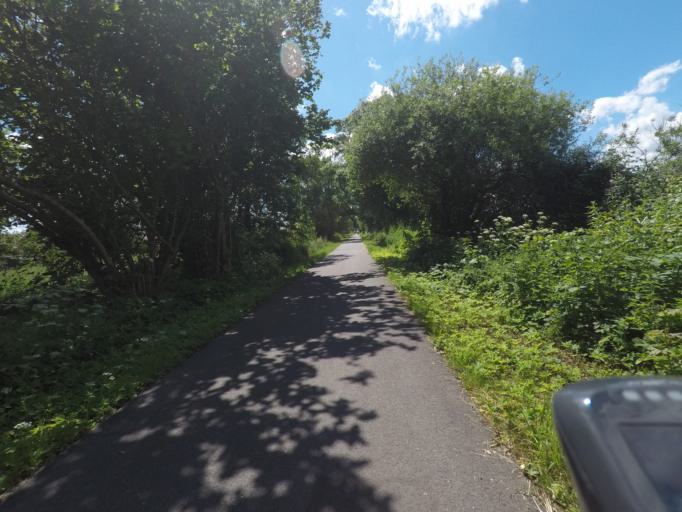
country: DE
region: Hamburg
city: Bergedorf
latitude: 53.4401
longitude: 10.2149
